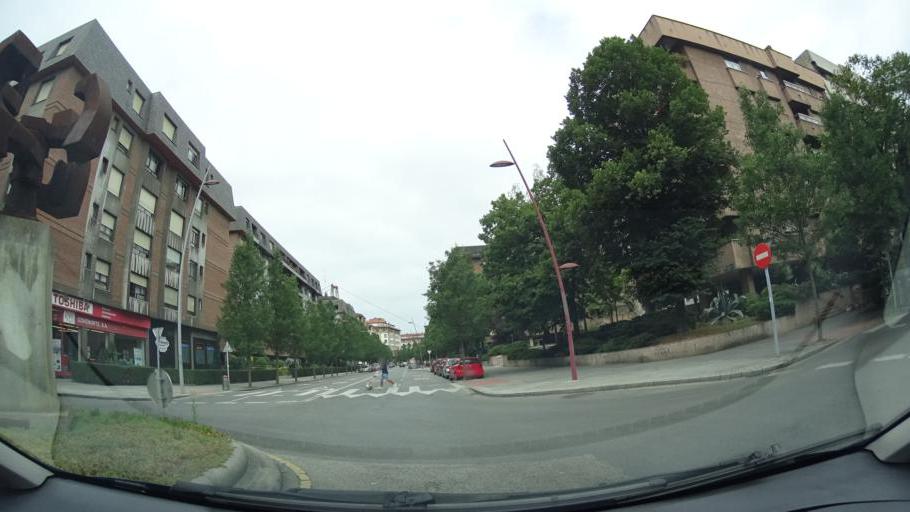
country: ES
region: Basque Country
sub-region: Bizkaia
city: Portugalete
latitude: 43.3219
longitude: -3.0133
